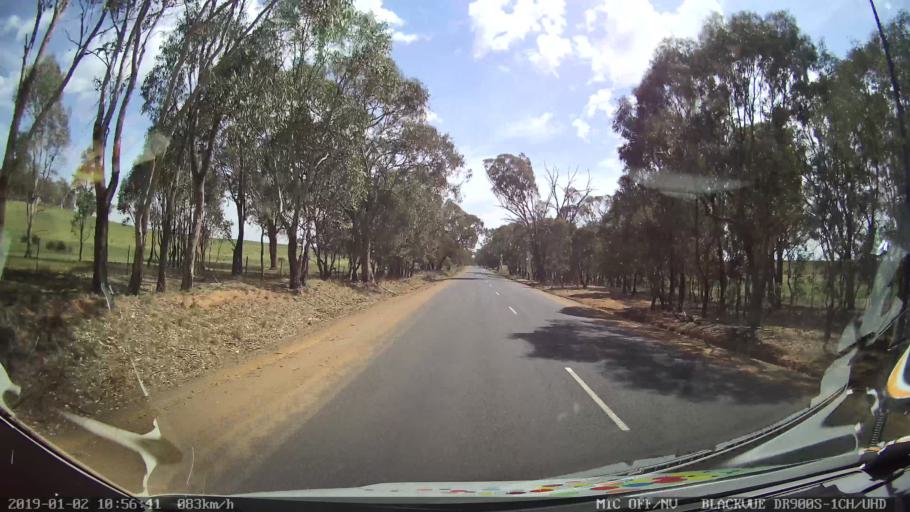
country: AU
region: New South Wales
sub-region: Cootamundra
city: Cootamundra
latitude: -34.6442
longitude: 148.2783
